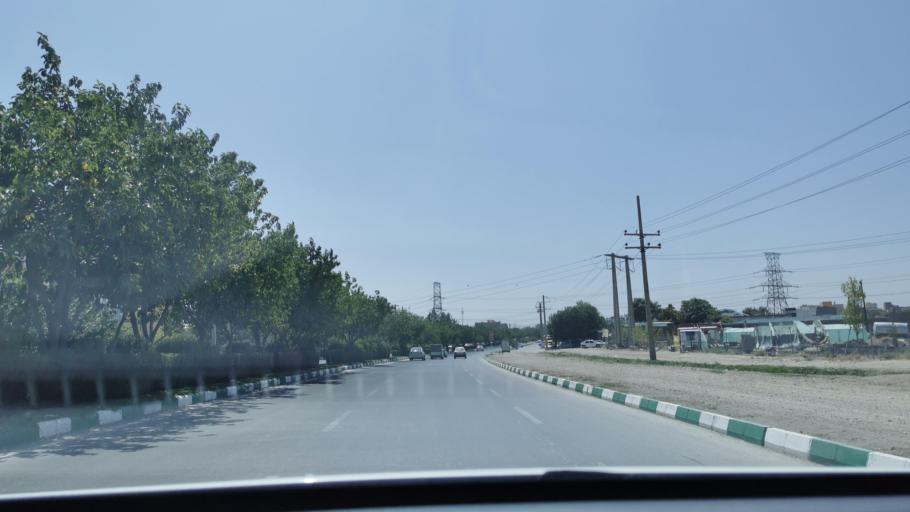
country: IR
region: Razavi Khorasan
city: Mashhad
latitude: 36.3520
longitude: 59.6302
